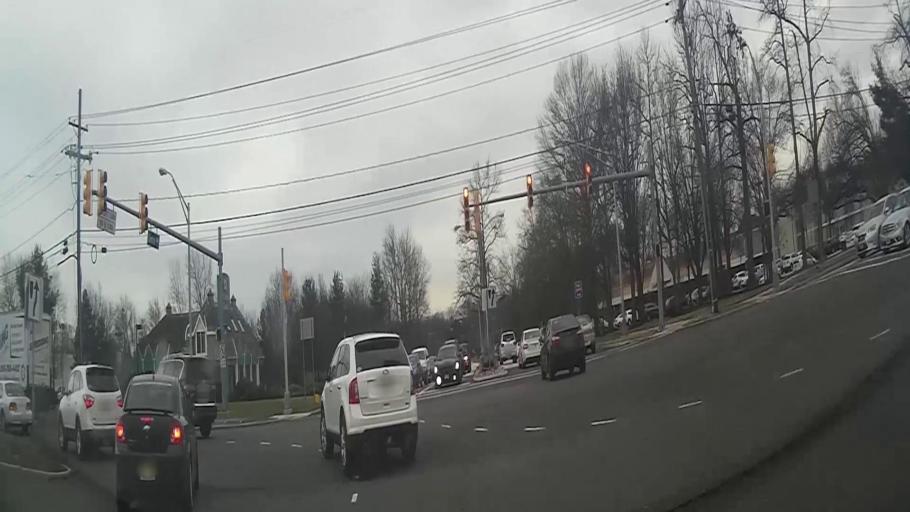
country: US
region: New Jersey
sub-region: Burlington County
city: Marlton
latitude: 39.8861
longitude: -74.9229
